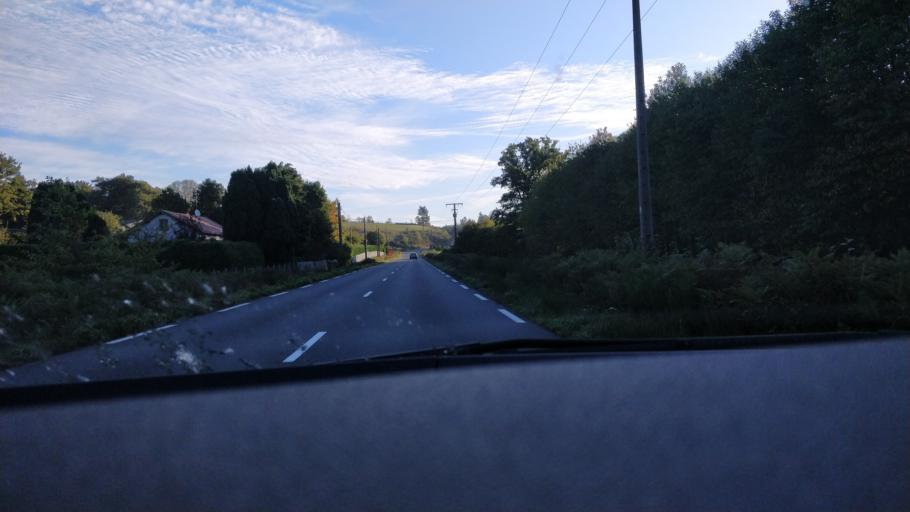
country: FR
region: Limousin
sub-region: Departement de la Haute-Vienne
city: Sauviat-sur-Vige
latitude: 45.9446
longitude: 1.6742
